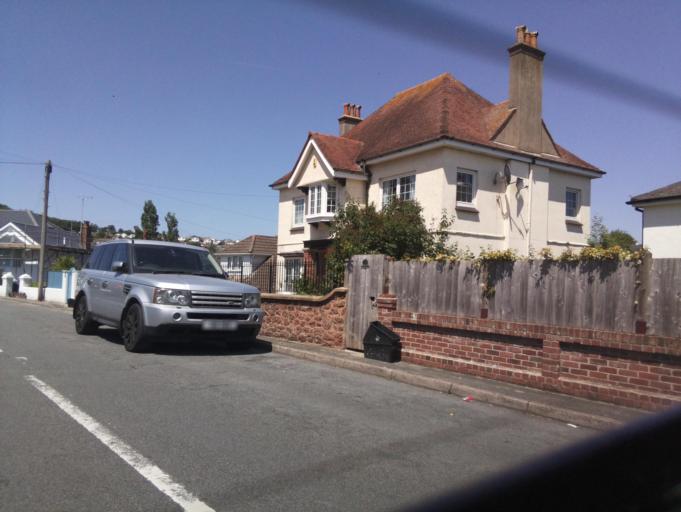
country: GB
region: England
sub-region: Borough of Torbay
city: Paignton
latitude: 50.4511
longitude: -3.5569
